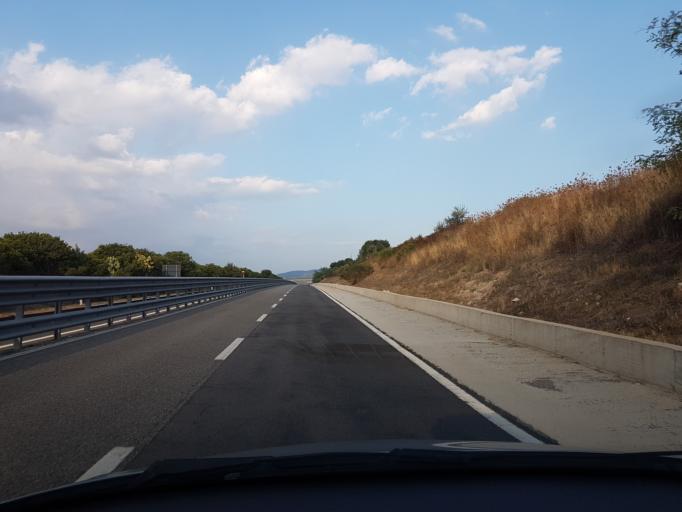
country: IT
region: Sardinia
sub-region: Provincia di Nuoro
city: Ottana
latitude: 40.2460
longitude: 9.0621
